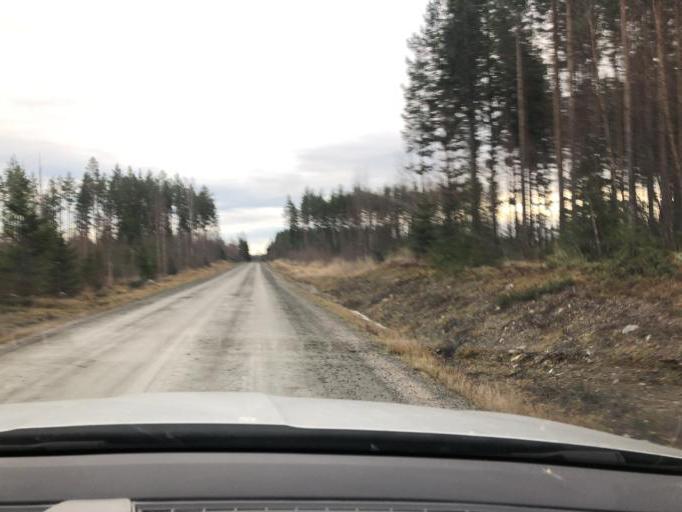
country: SE
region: Gaevleborg
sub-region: Hudiksvalls Kommun
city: Sorforsa
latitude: 61.6480
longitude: 16.9343
